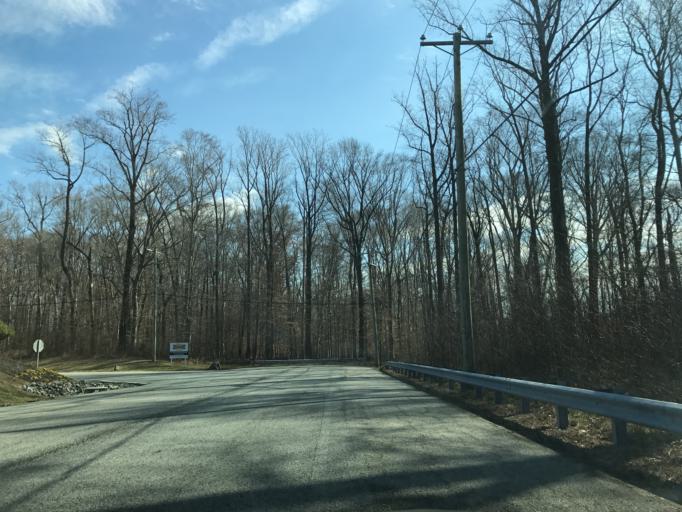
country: US
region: Maryland
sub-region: Cecil County
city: Perryville
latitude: 39.5575
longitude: -76.0606
